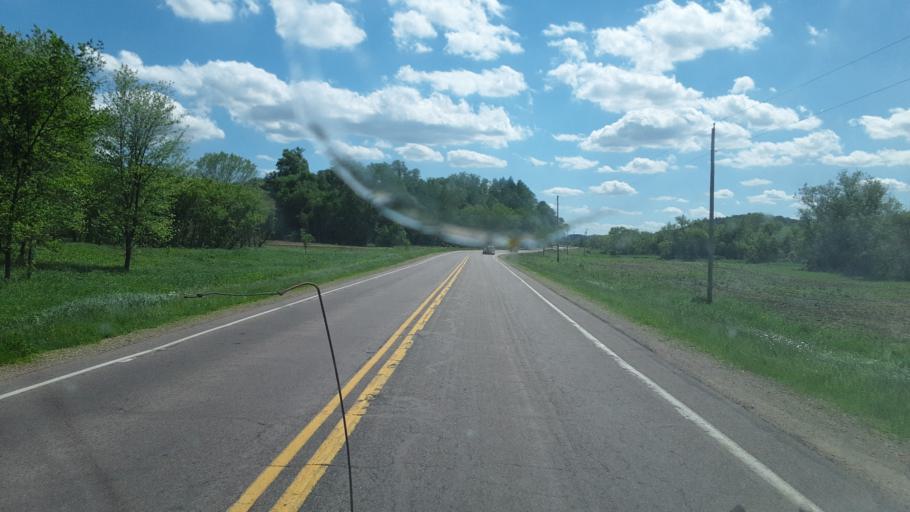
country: US
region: Wisconsin
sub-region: Richland County
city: Richland Center
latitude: 43.3564
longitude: -90.2701
